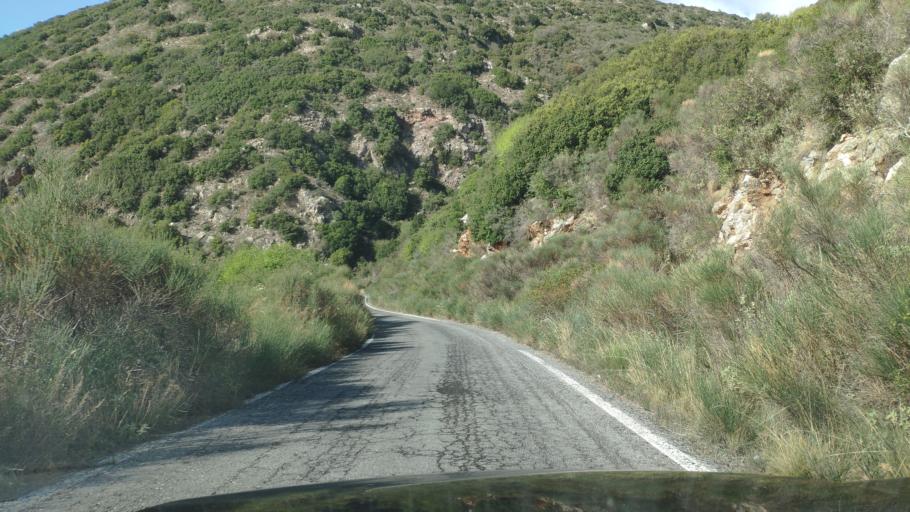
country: GR
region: Peloponnese
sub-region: Nomos Arkadias
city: Dimitsana
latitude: 37.5738
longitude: 22.0161
